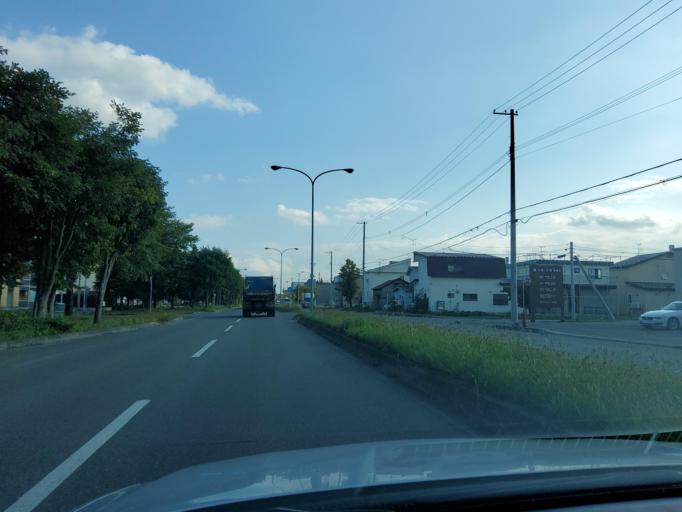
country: JP
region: Hokkaido
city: Obihiro
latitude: 42.9073
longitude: 143.2138
